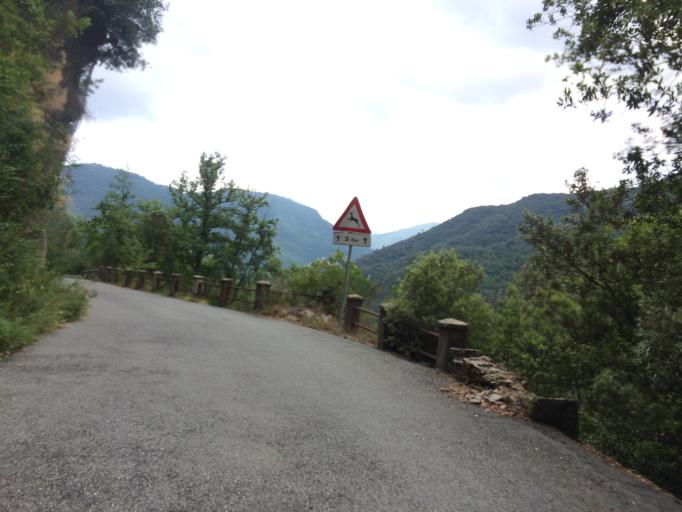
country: IT
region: Liguria
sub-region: Provincia di Imperia
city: Castel Vittorio
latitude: 43.9416
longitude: 7.6876
